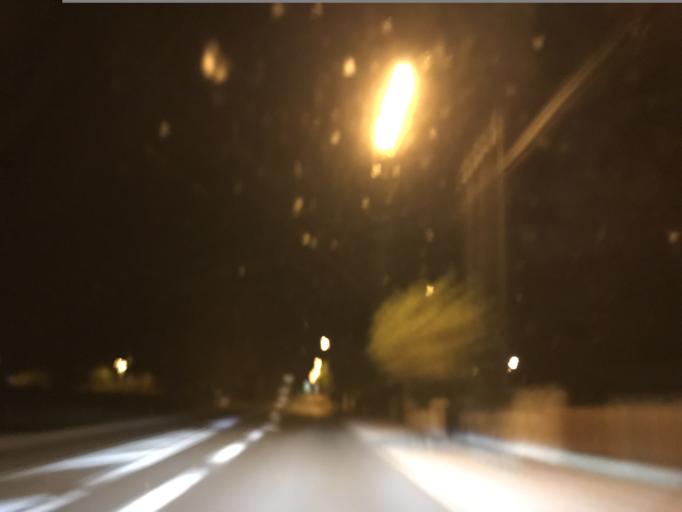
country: FR
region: Auvergne
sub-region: Departement du Puy-de-Dome
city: Puy-Guillaume
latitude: 45.9518
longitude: 3.4796
